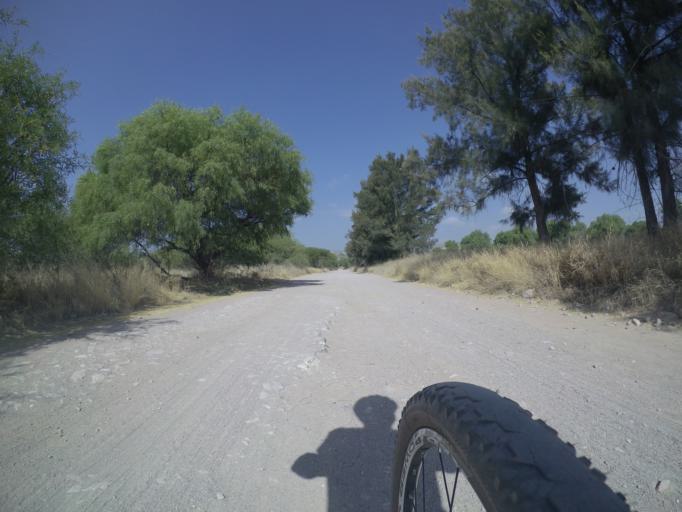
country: MX
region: Aguascalientes
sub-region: Jesus Maria
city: Paseos de las Haciendas [Fraccionamiento]
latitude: 21.9999
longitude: -102.3470
